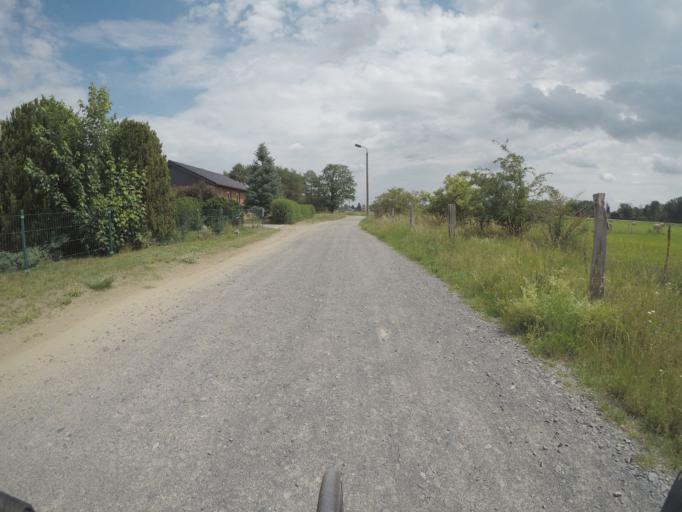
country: DE
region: Brandenburg
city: Kremmen
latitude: 52.7694
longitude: 13.0274
